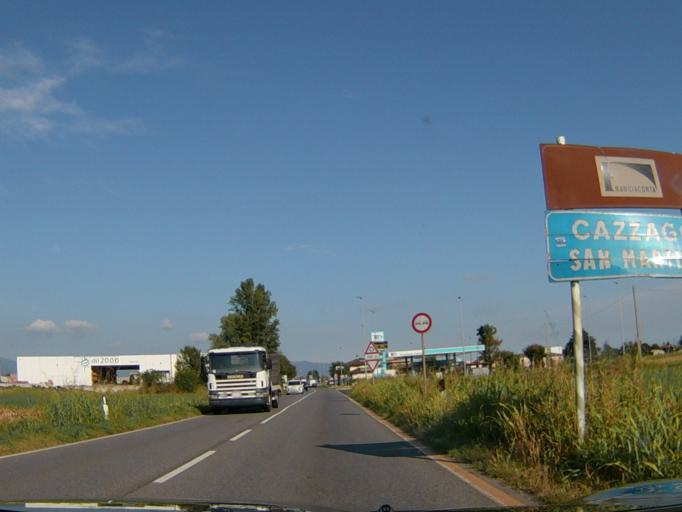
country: IT
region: Lombardy
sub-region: Provincia di Brescia
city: Lodetto
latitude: 45.5584
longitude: 10.0376
